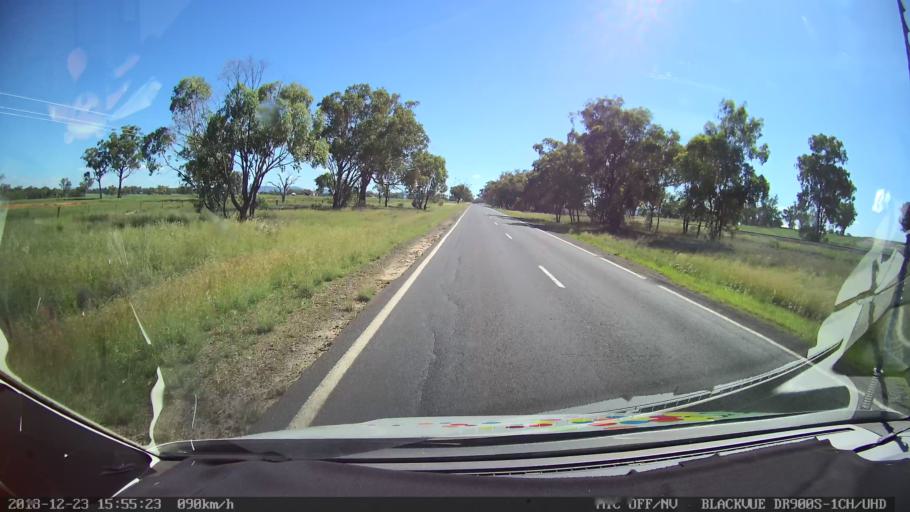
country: AU
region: New South Wales
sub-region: Tamworth Municipality
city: Phillip
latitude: -31.1549
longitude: 150.8690
